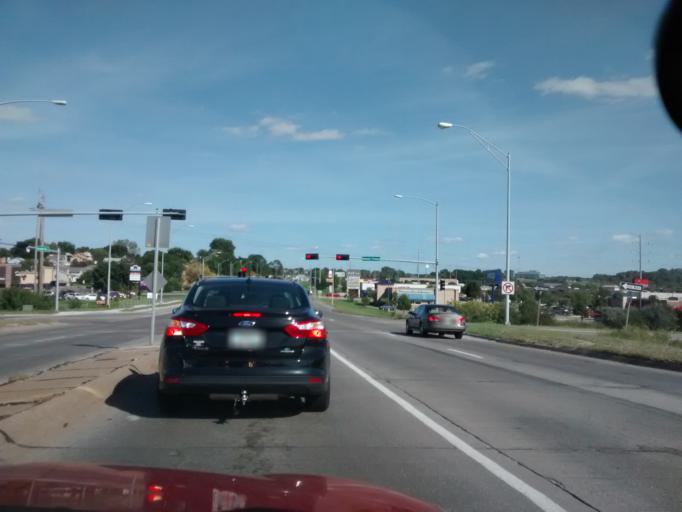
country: US
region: Nebraska
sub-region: Sarpy County
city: Offutt Air Force Base
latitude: 41.1588
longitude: -95.9381
